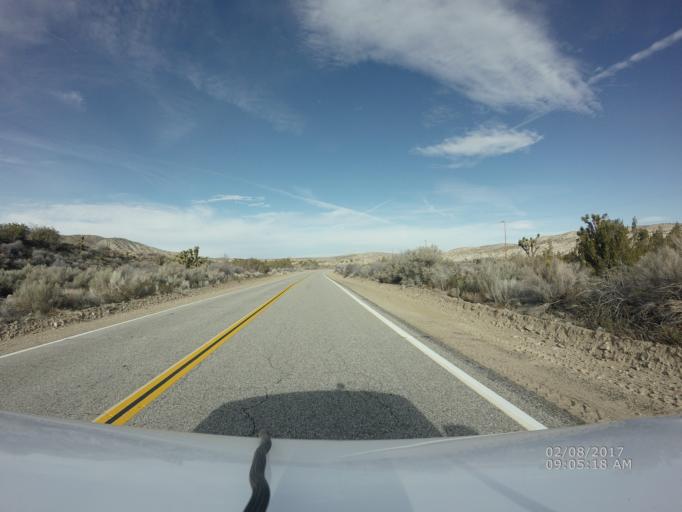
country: US
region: California
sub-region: Los Angeles County
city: Littlerock
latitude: 34.4415
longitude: -117.8459
